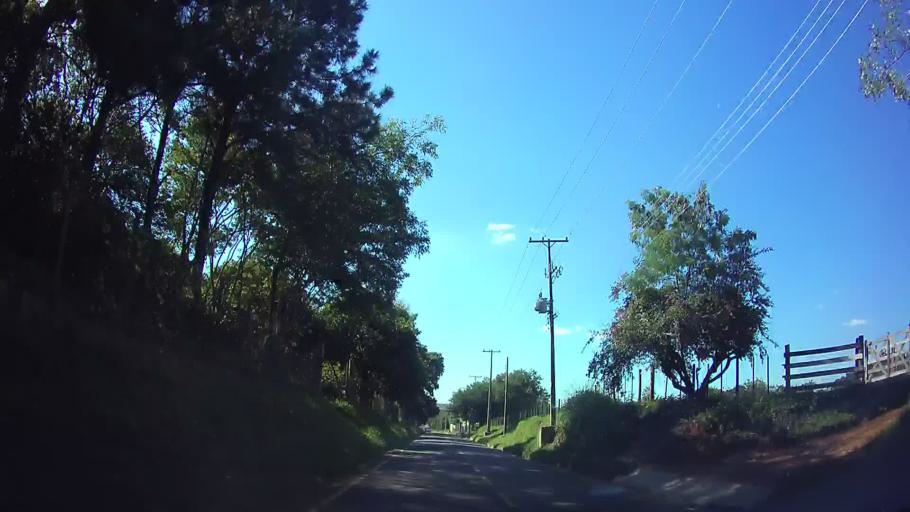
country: PY
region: Central
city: Limpio
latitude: -25.2020
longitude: -57.4789
